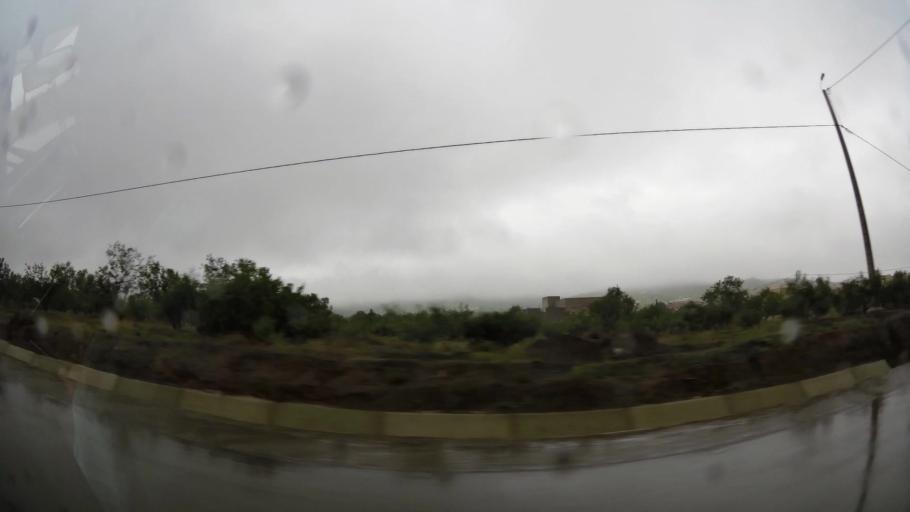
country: MA
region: Oriental
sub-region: Nador
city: Midar
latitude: 34.8514
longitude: -3.7219
